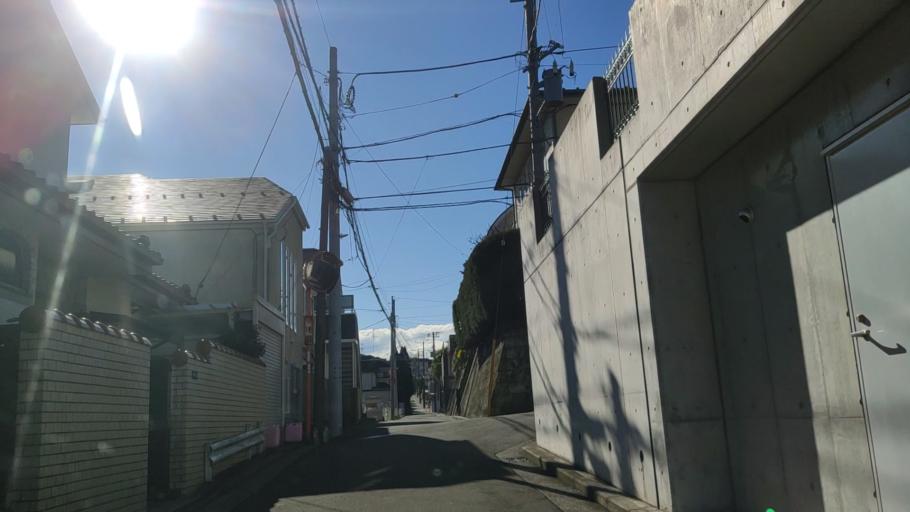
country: JP
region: Kanagawa
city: Yokohama
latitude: 35.4259
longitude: 139.6550
